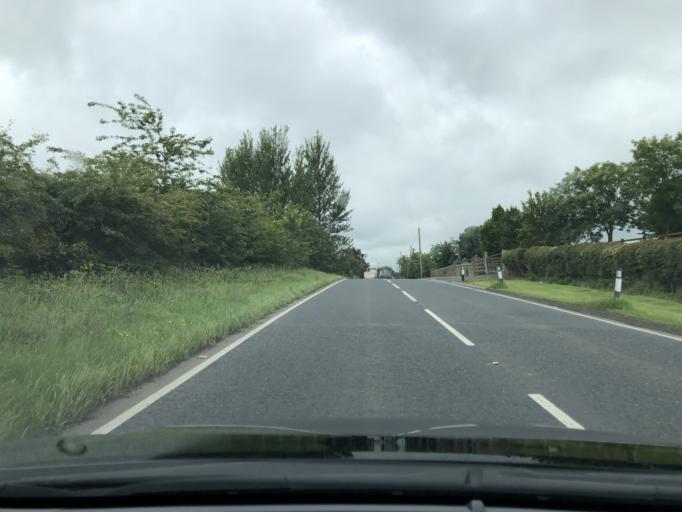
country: GB
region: Northern Ireland
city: Ballynahinch
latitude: 54.3784
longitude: -5.8692
